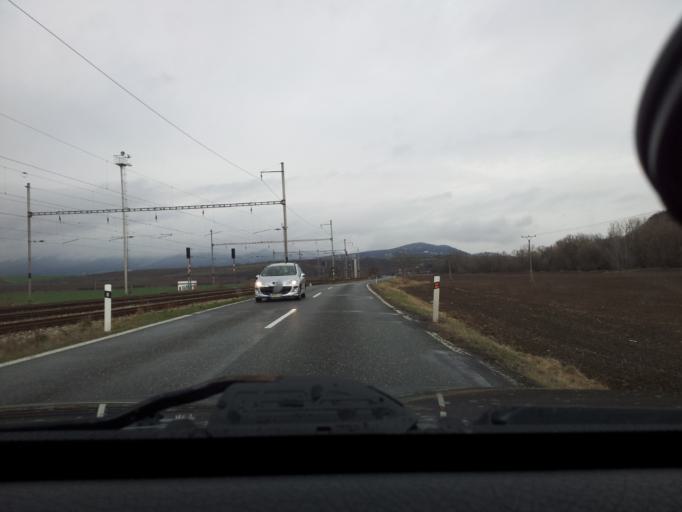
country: SK
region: Nitriansky
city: Tlmace
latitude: 48.3155
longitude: 18.5387
